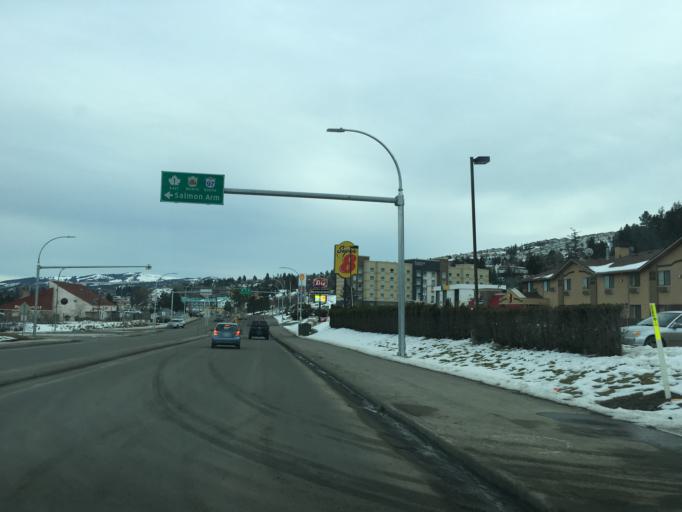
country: CA
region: British Columbia
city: Kamloops
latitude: 50.6526
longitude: -120.3824
